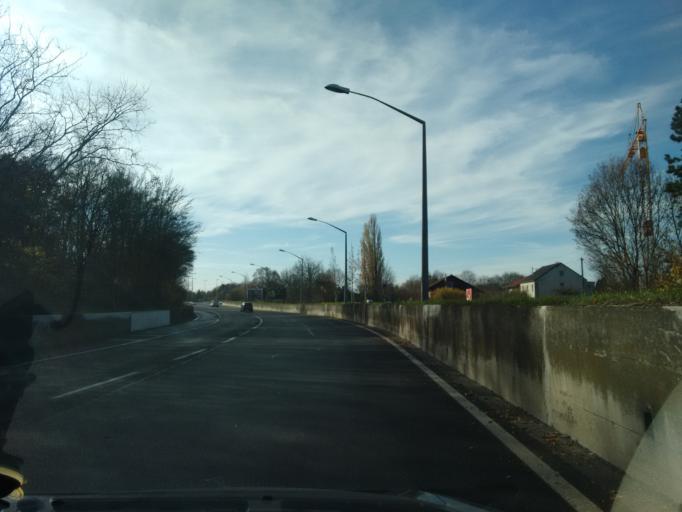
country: AT
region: Upper Austria
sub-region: Linz Stadt
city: Linz
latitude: 48.2628
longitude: 14.3006
